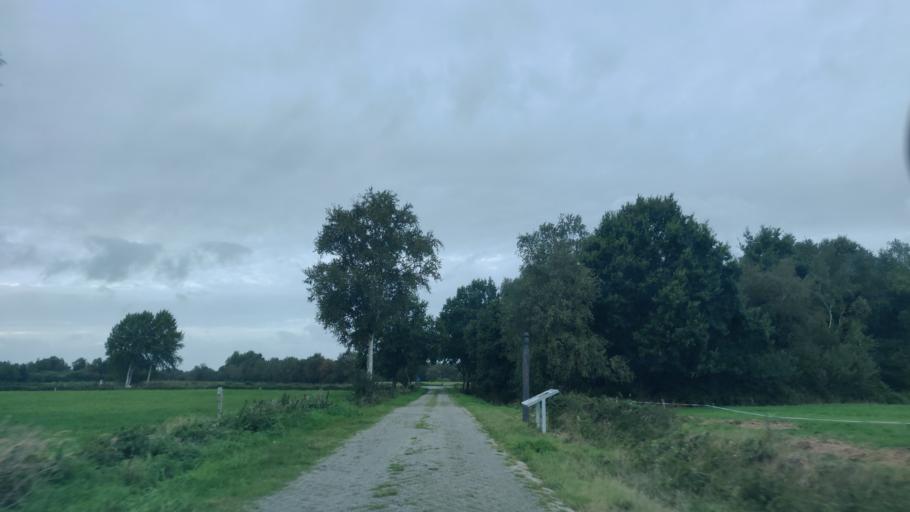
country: DE
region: Lower Saxony
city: Aurich
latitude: 53.5305
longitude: 7.4723
